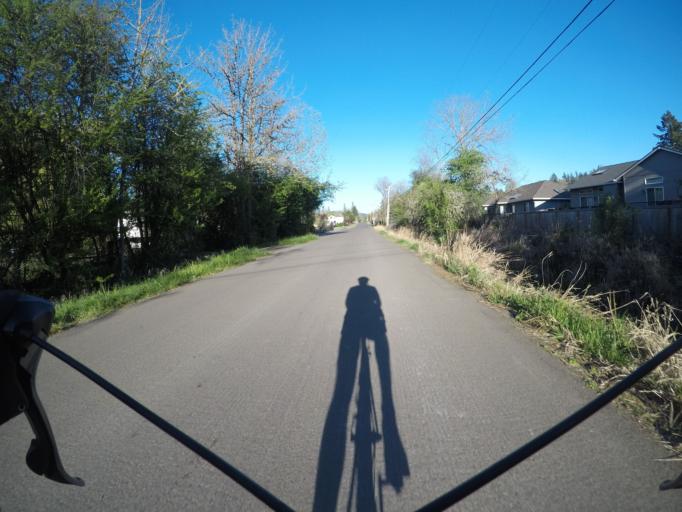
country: US
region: Oregon
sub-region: Washington County
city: Oak Hills
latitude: 45.5215
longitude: -122.8324
